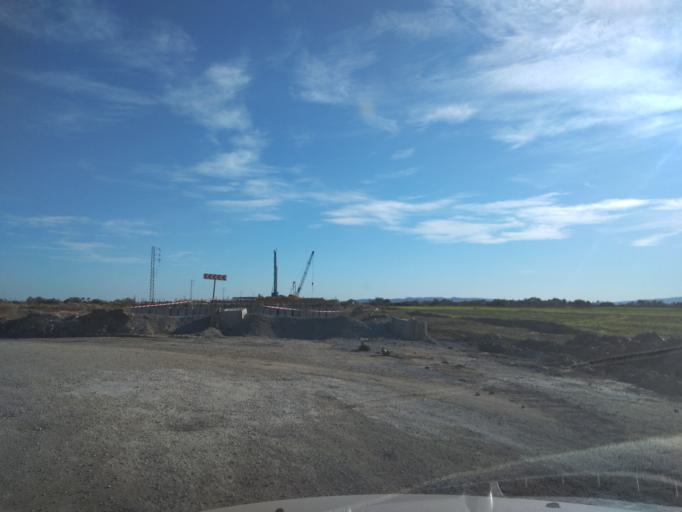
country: TN
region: Ariana
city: Qal'at al Andalus
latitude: 37.0258
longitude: 10.1392
